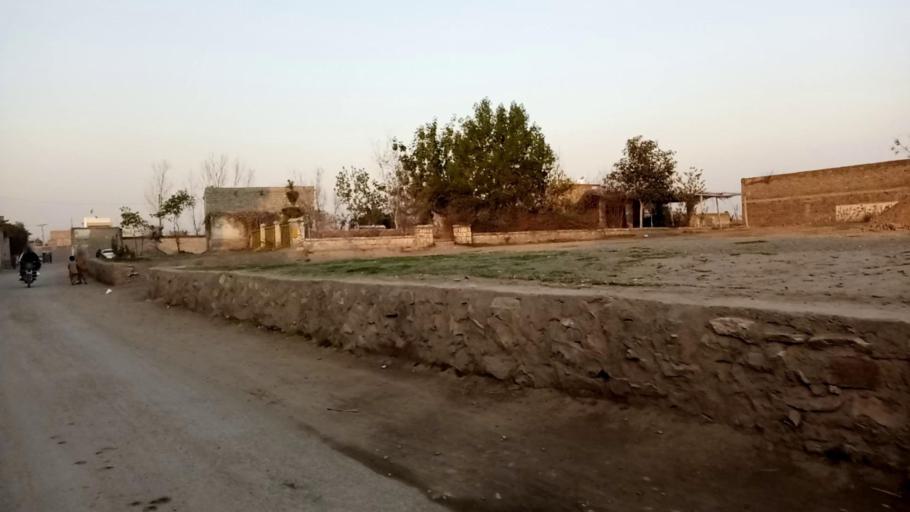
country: PK
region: Khyber Pakhtunkhwa
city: Peshawar
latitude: 34.0456
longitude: 71.4532
